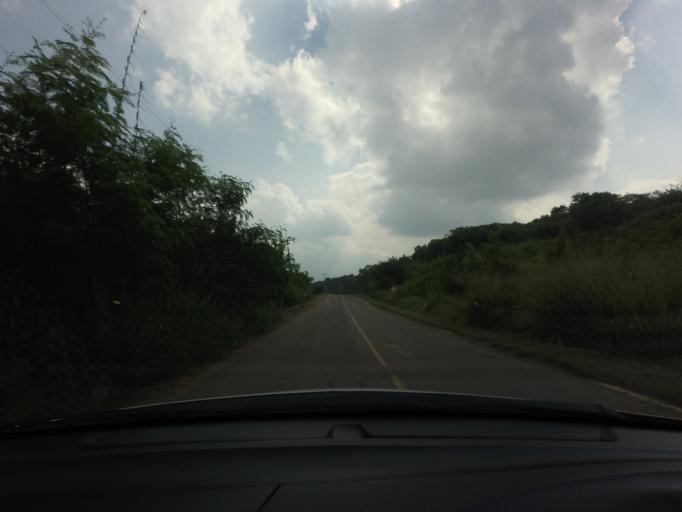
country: TH
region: Nakhon Ratchasima
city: Pak Chong
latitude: 14.5171
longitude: 101.5732
